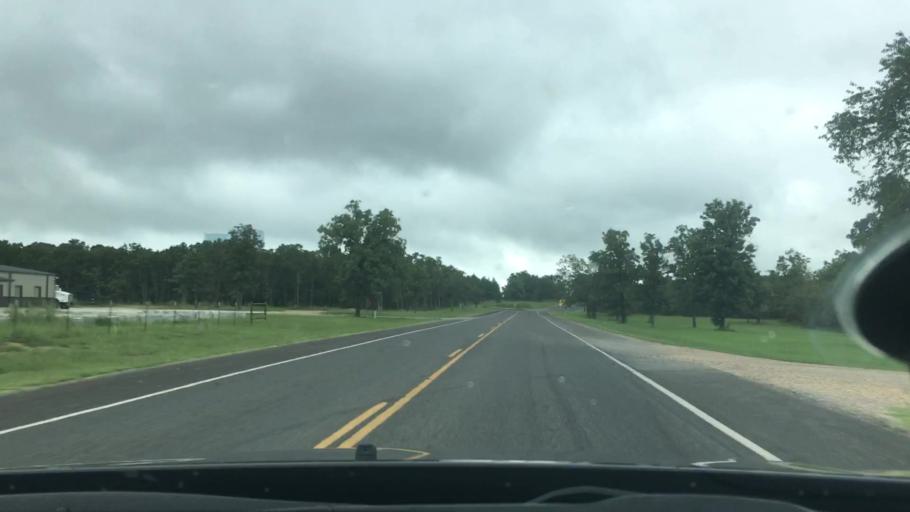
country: US
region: Oklahoma
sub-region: Sequoyah County
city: Vian
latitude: 35.5635
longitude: -94.9832
